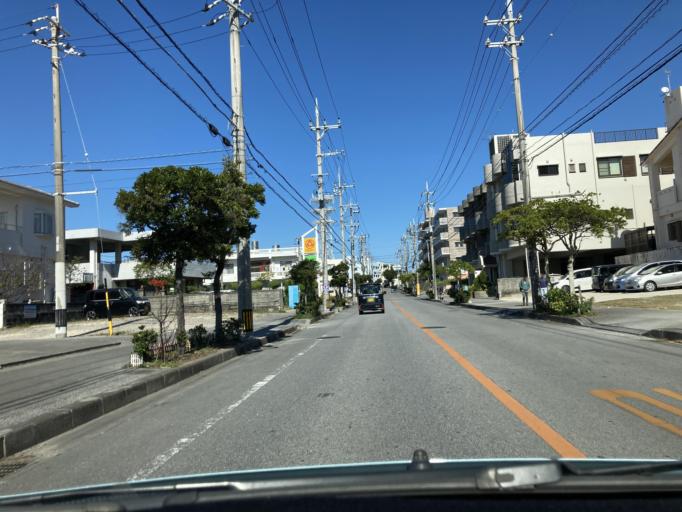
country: JP
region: Okinawa
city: Okinawa
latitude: 26.3234
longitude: 127.8015
